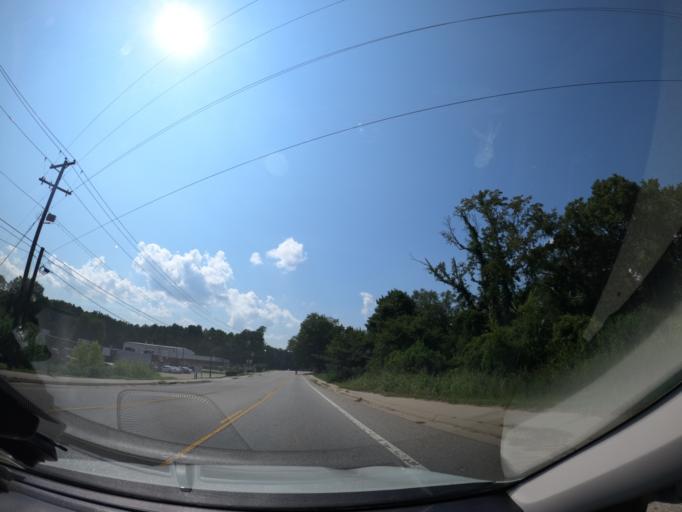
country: US
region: South Carolina
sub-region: Richland County
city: Forest Acres
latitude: 33.9346
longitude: -80.9725
